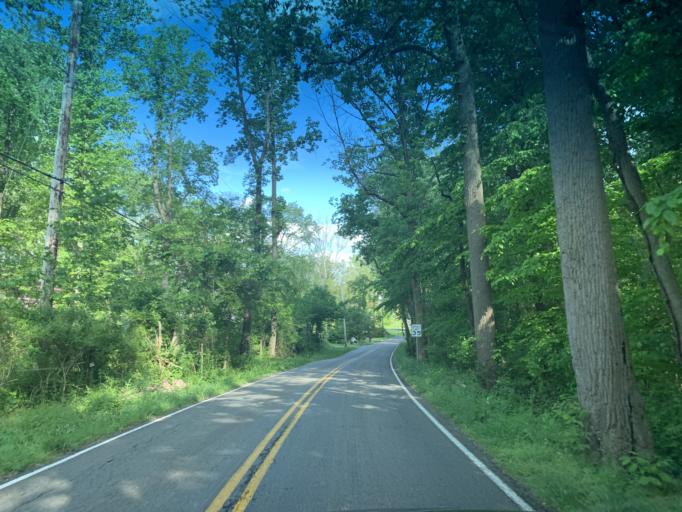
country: US
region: Maryland
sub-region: Cecil County
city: Rising Sun
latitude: 39.6963
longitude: -76.1565
